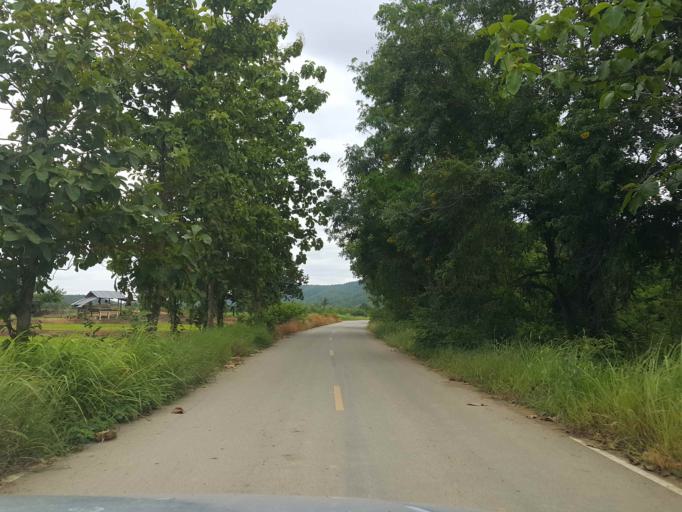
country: TH
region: Sukhothai
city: Thung Saliam
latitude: 17.3341
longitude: 99.4395
